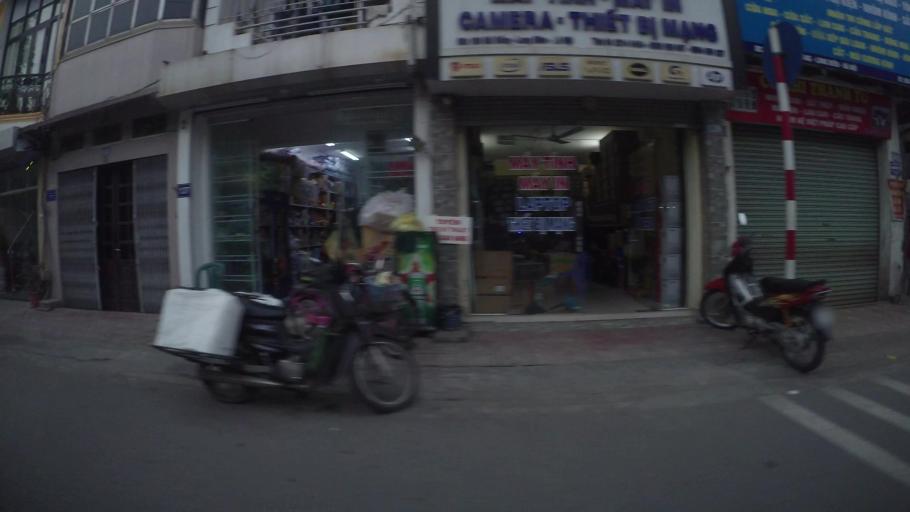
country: VN
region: Ha Noi
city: Trau Quy
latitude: 21.0367
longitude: 105.9114
